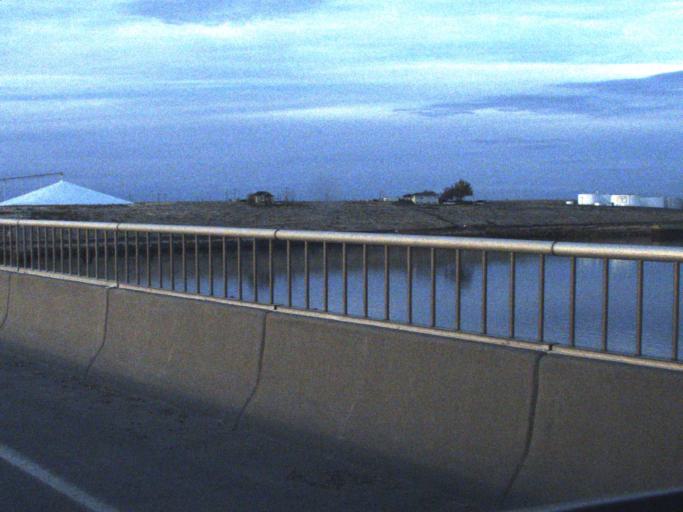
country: US
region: Washington
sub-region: Walla Walla County
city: Burbank
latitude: 46.2145
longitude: -119.0204
